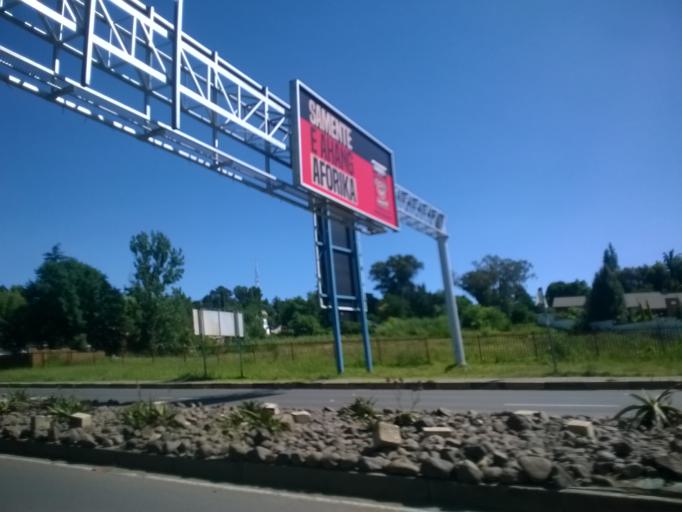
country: LS
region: Maseru
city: Maseru
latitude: -29.3107
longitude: 27.4759
